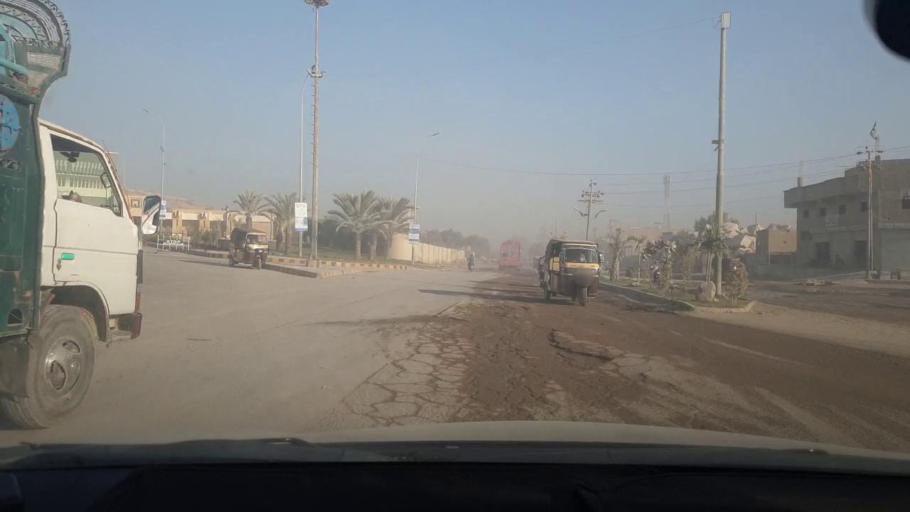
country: PK
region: Sindh
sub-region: Karachi District
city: Karachi
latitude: 24.9705
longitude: 67.0396
